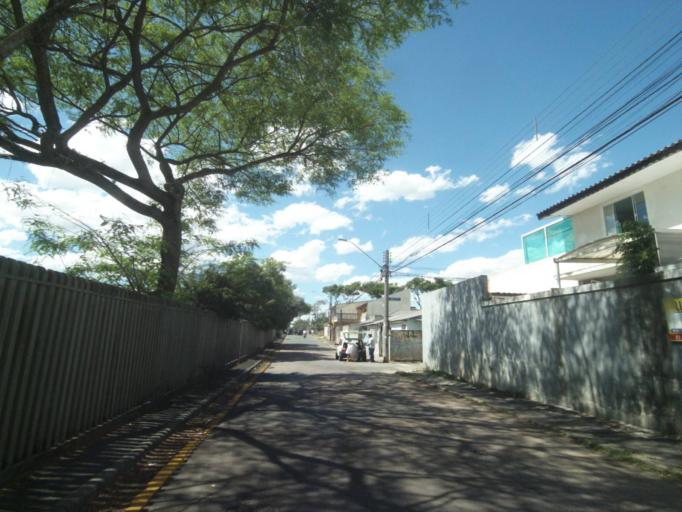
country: BR
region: Parana
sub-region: Curitiba
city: Curitiba
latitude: -25.5045
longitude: -49.3233
